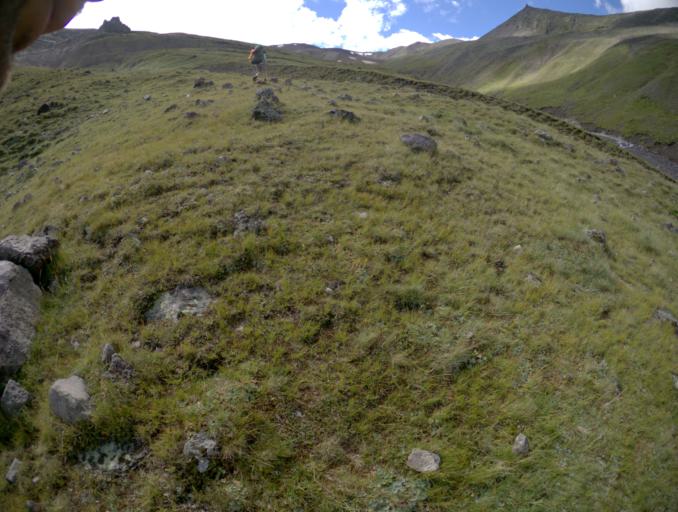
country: RU
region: Kabardino-Balkariya
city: Terskol
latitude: 43.3939
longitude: 42.3617
